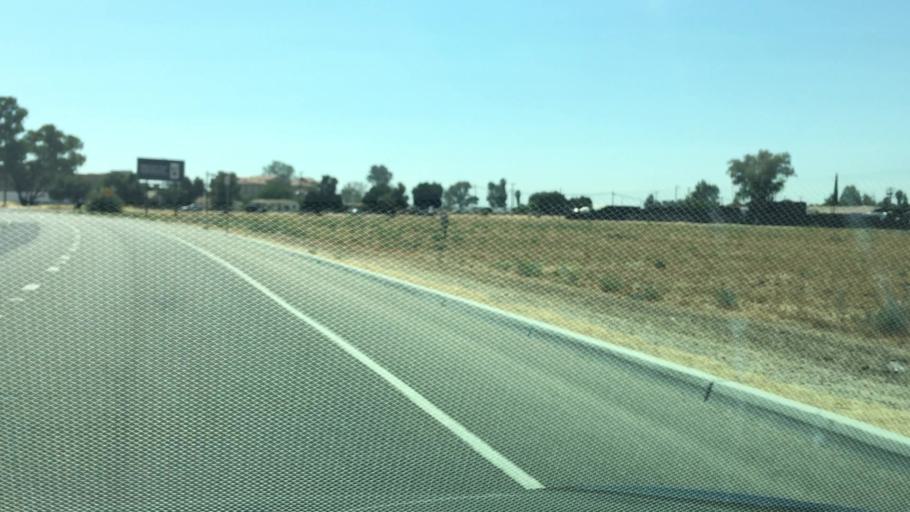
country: US
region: California
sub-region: Fresno County
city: Biola
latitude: 36.8362
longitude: -119.9138
